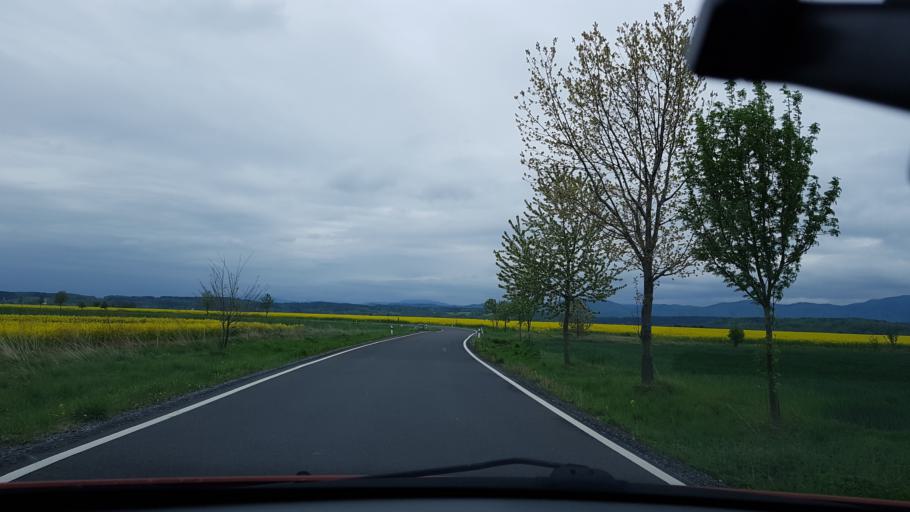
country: CZ
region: Olomoucky
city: Vidnava
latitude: 50.3813
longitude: 17.1420
